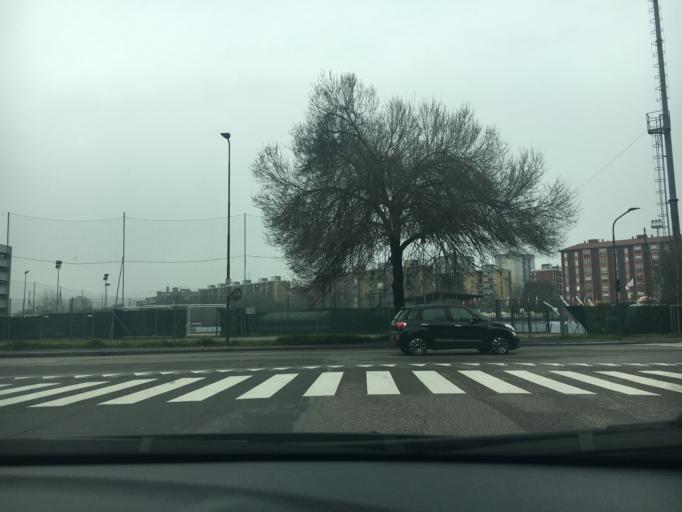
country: IT
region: Lombardy
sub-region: Citta metropolitana di Milano
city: Pero
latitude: 45.4935
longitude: 9.1034
